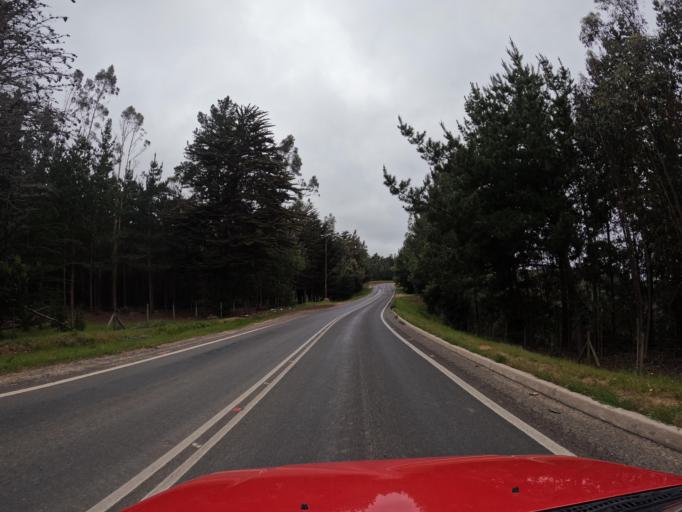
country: CL
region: O'Higgins
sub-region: Provincia de Colchagua
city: Santa Cruz
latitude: -34.5914
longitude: -72.0157
